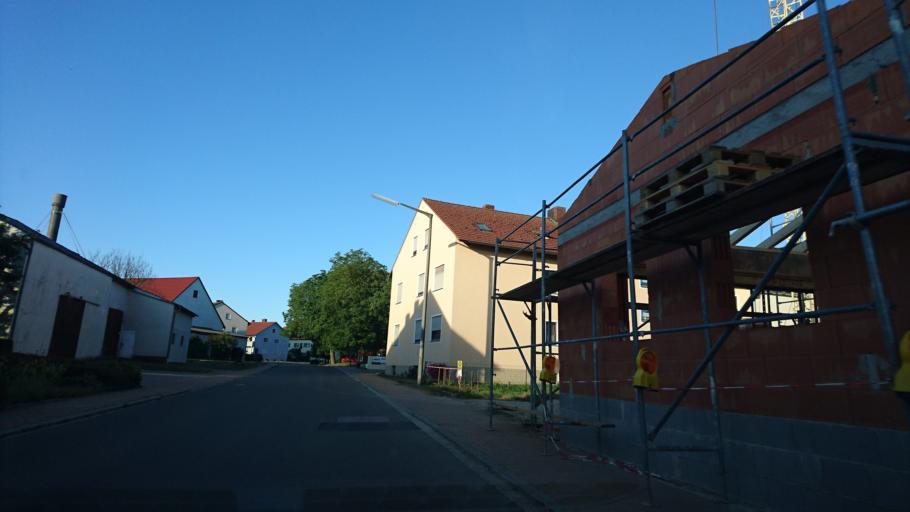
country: DE
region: Bavaria
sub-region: Regierungsbezirk Mittelfranken
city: Burgsalach
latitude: 49.0350
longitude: 11.1016
